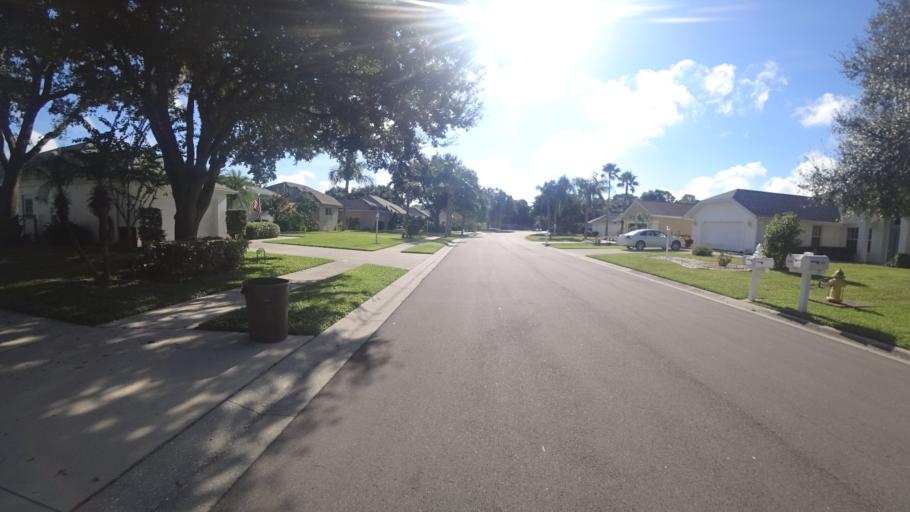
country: US
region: Florida
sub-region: Manatee County
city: Ellenton
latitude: 27.5951
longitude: -82.4916
